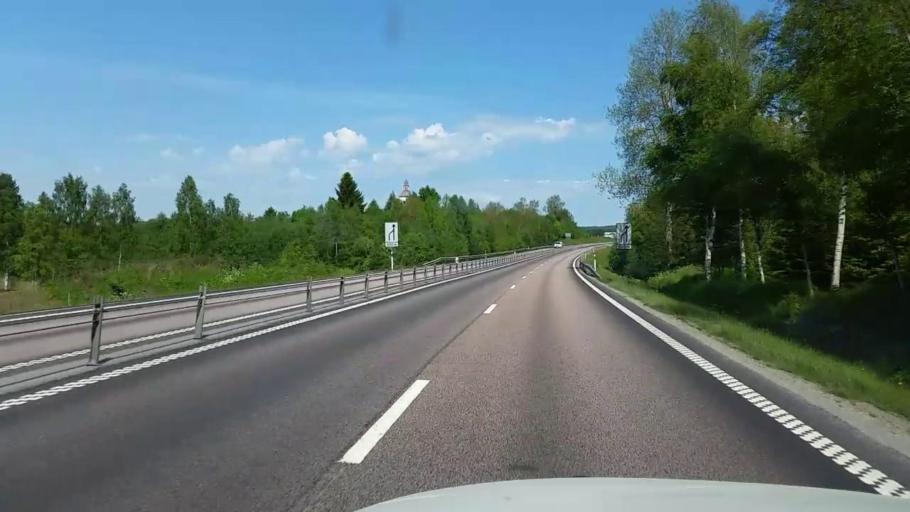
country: SE
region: Gaevleborg
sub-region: Hudiksvalls Kommun
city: Hudiksvall
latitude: 61.7501
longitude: 17.0797
